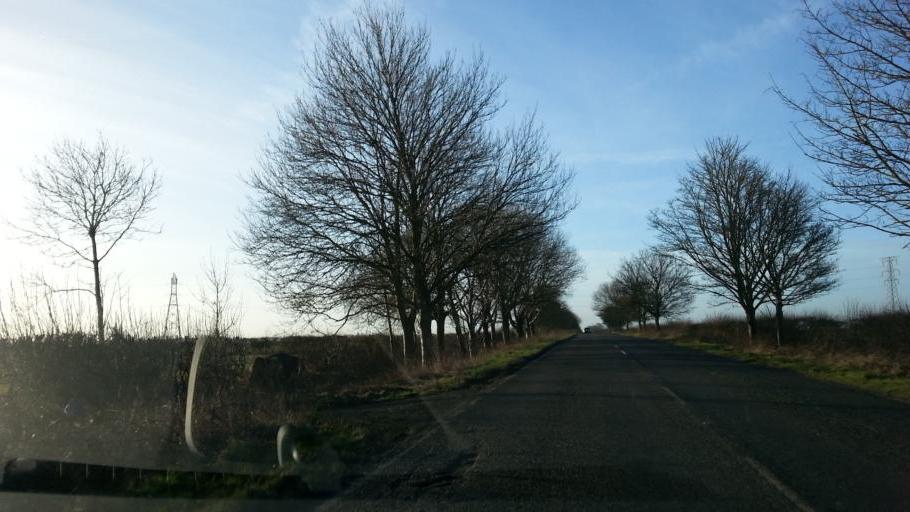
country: GB
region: England
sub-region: Lincolnshire
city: Grantham
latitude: 52.9270
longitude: -0.5718
